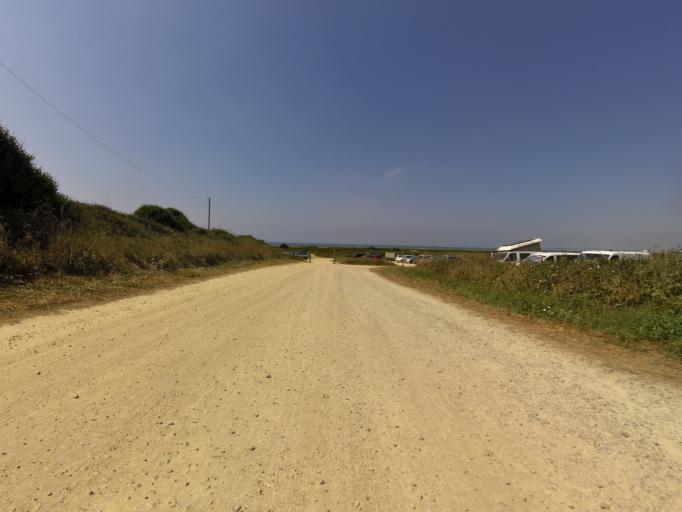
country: FR
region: Brittany
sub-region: Departement du Finistere
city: Pouldreuzic
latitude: 47.9001
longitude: -4.3664
